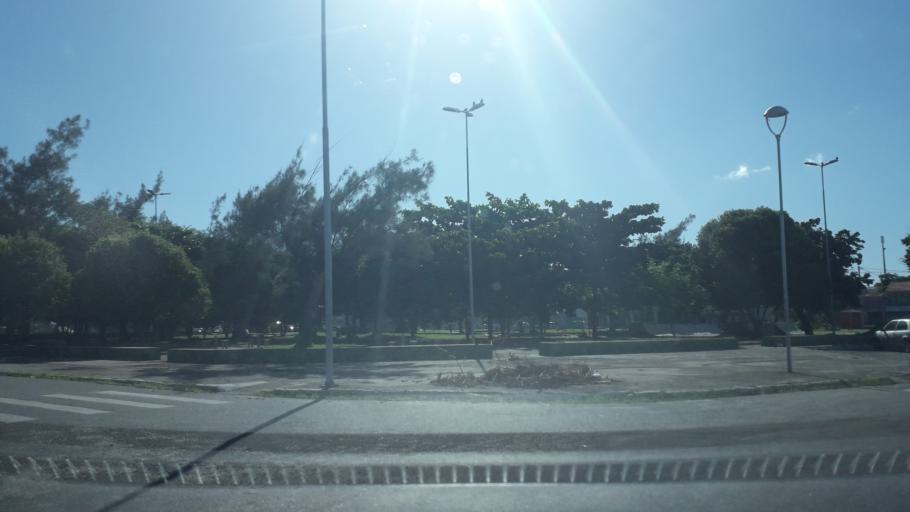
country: BR
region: Alagoas
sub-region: Maceio
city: Maceio
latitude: -9.6689
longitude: -35.7441
